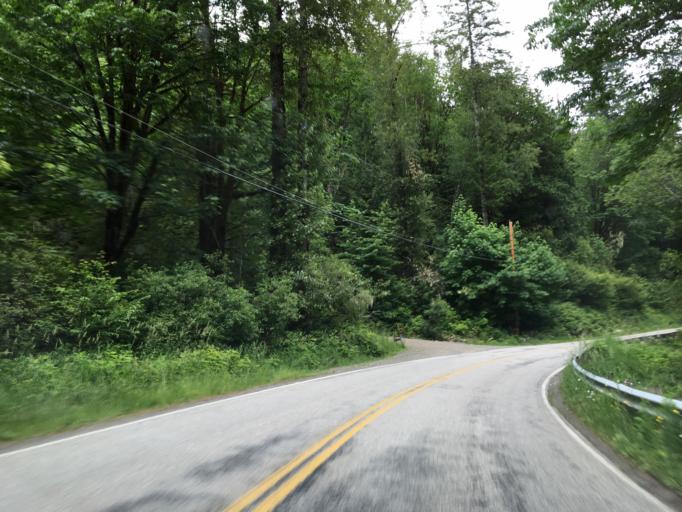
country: US
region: Washington
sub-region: Whatcom County
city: Peaceful Valley
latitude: 48.9297
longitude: -122.0779
